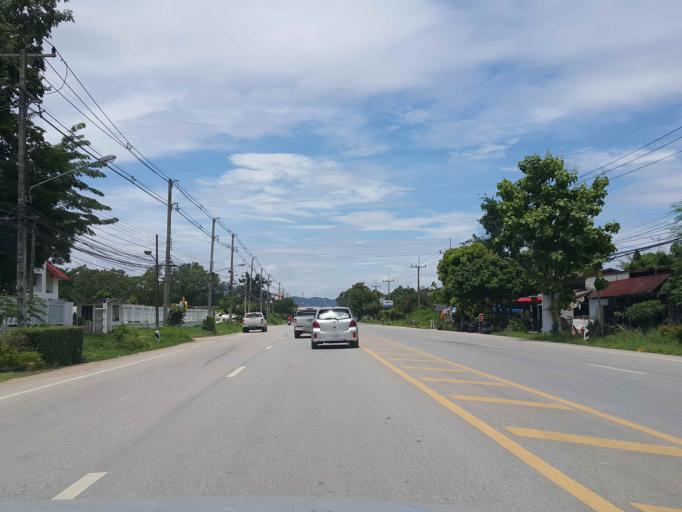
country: TH
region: Sukhothai
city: Ban Na
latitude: 17.0152
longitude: 99.7436
